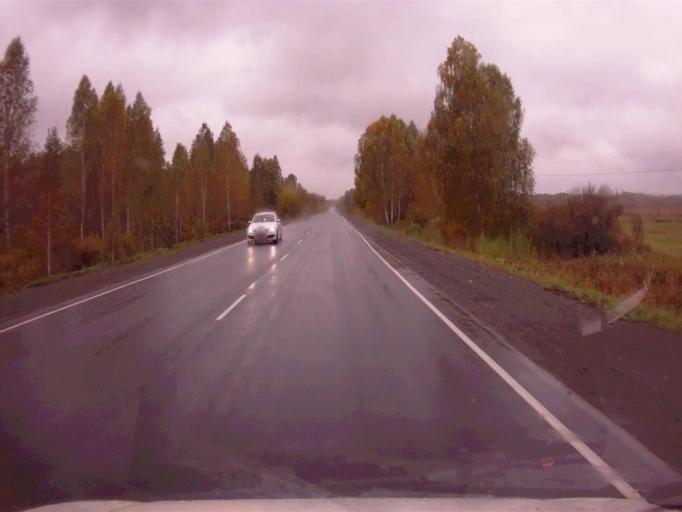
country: RU
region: Chelyabinsk
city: Argayash
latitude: 55.4790
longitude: 60.7972
